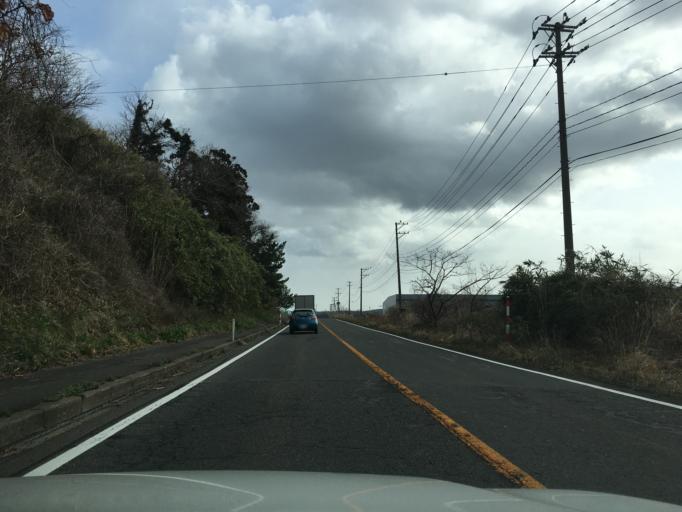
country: JP
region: Yamagata
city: Yuza
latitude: 39.2788
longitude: 139.9311
